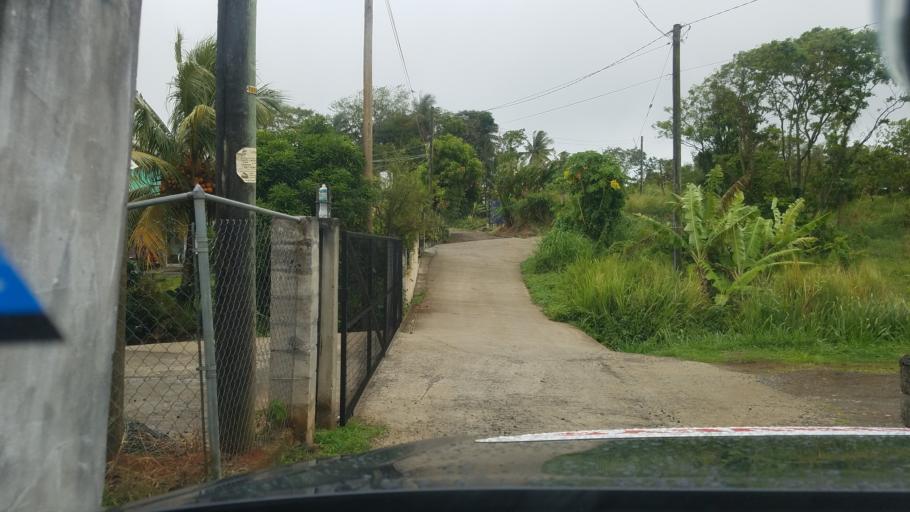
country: LC
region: Castries Quarter
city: Bisee
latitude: 14.0205
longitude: -60.9335
